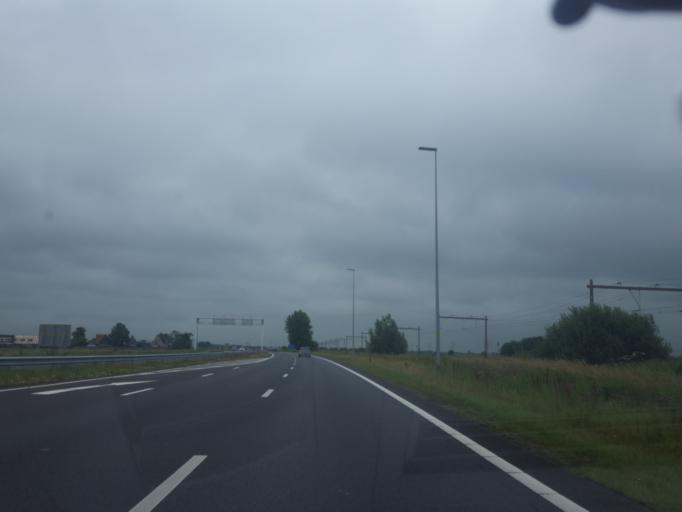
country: NL
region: Friesland
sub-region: Gemeente Leeuwarden
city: Wirdum
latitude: 53.1508
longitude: 5.7928
